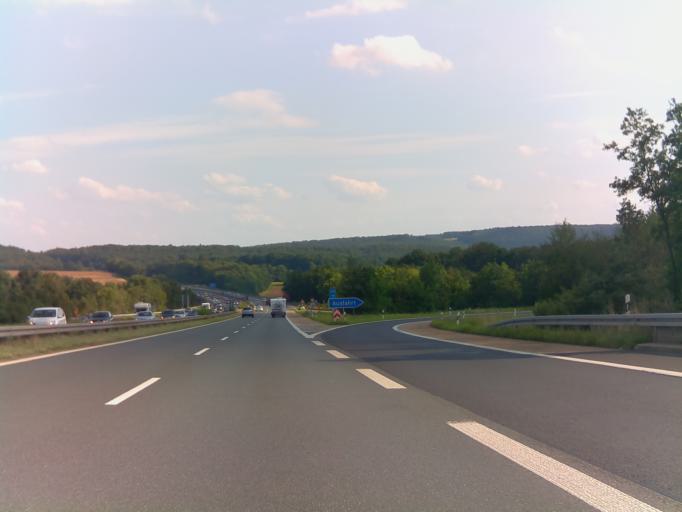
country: DE
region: Bavaria
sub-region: Regierungsbezirk Unterfranken
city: Oberthulba
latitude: 50.1983
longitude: 9.9389
